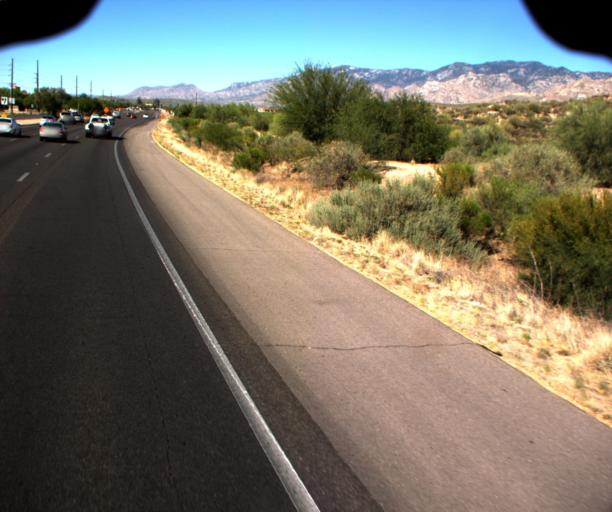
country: US
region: Arizona
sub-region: Pima County
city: Oro Valley
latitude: 32.3934
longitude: -110.9620
